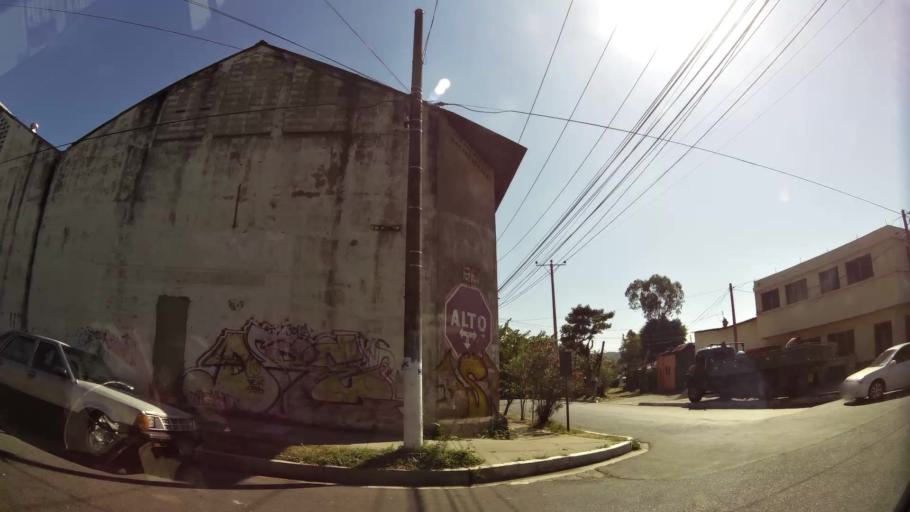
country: SV
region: La Libertad
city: Santa Tecla
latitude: 13.6698
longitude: -89.2849
